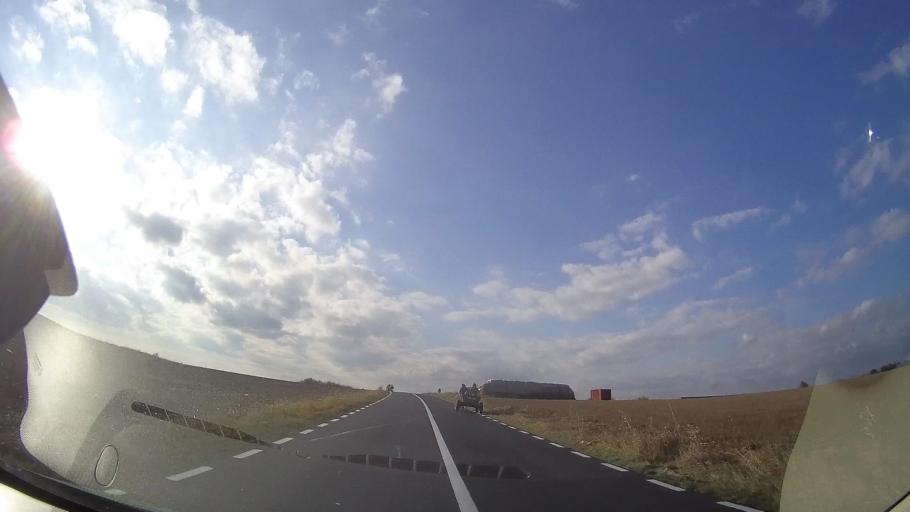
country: RO
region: Constanta
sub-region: Comuna Limanu
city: Limanu
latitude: 43.8249
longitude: 28.4972
